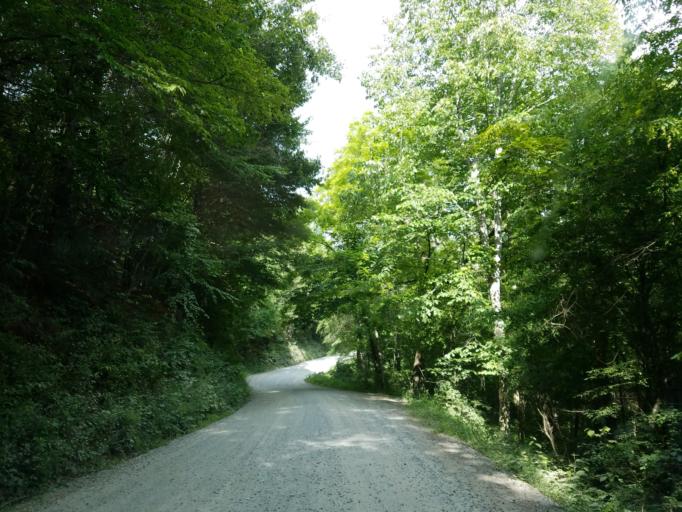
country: US
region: Georgia
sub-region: Fannin County
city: Blue Ridge
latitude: 34.7921
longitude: -84.2513
